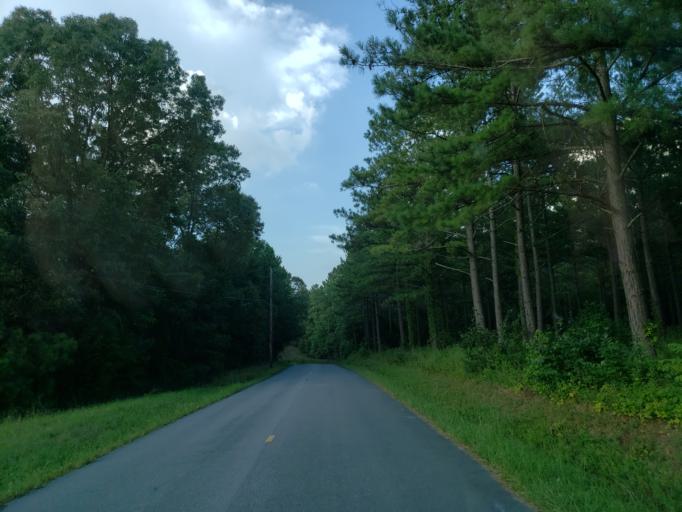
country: US
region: Georgia
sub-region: Bartow County
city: Euharlee
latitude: 34.0866
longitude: -84.9349
